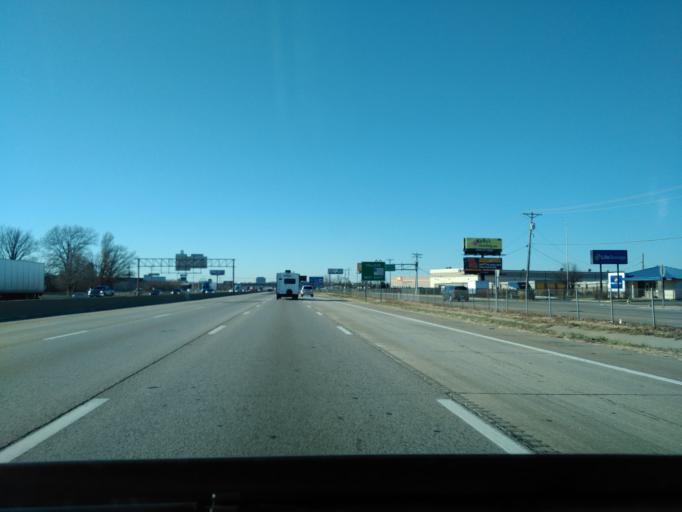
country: US
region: Missouri
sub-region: Saint Louis County
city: Fenton
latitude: 38.5429
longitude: -90.4469
